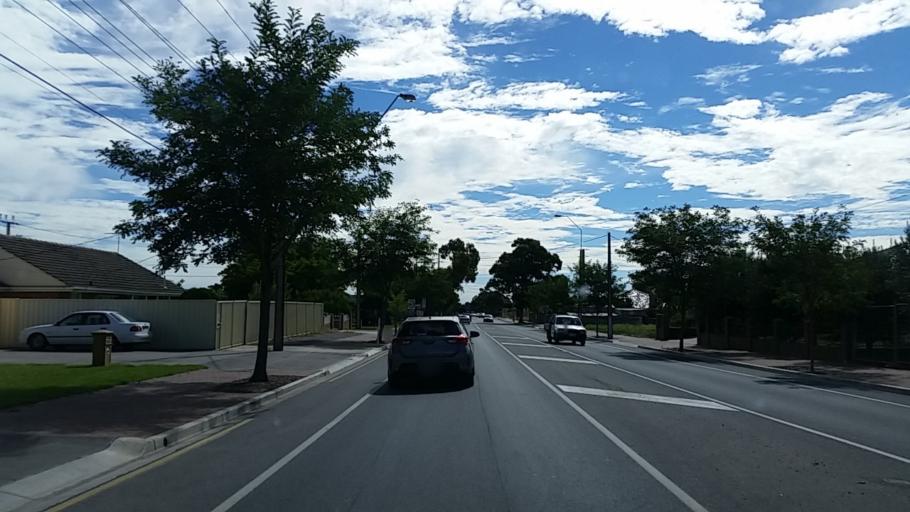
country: AU
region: South Australia
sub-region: Campbelltown
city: Paradise
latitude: -34.8759
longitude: 138.6824
